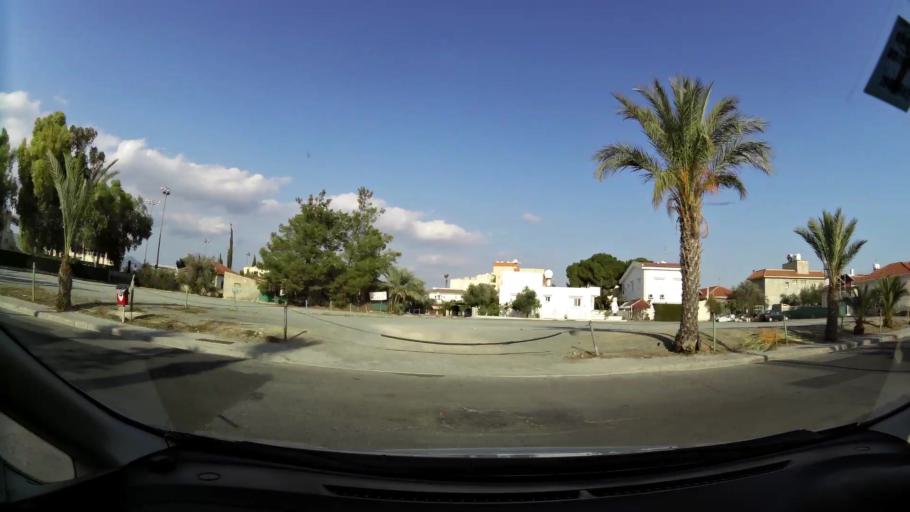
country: CY
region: Lefkosia
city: Nicosia
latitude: 35.1744
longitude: 33.3278
